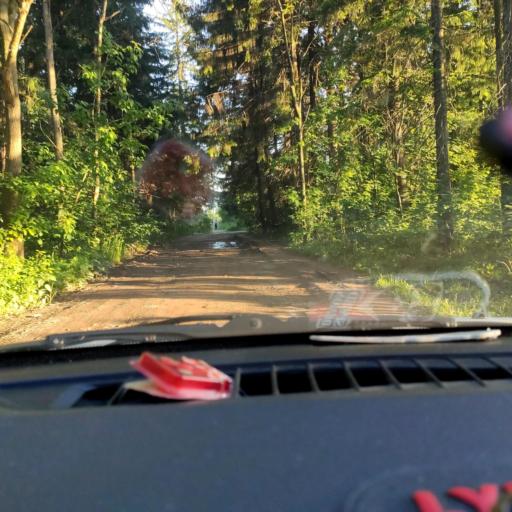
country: RU
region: Perm
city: Froly
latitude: 57.9426
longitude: 56.1984
